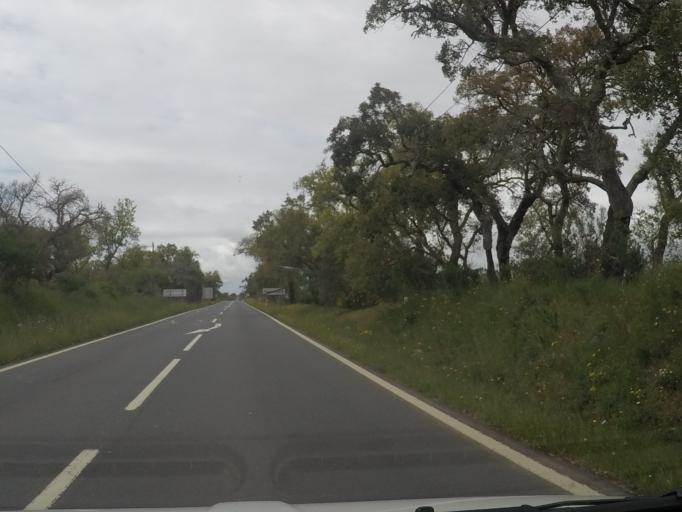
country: PT
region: Setubal
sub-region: Santiago do Cacem
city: Cercal
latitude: 37.8526
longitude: -8.7115
